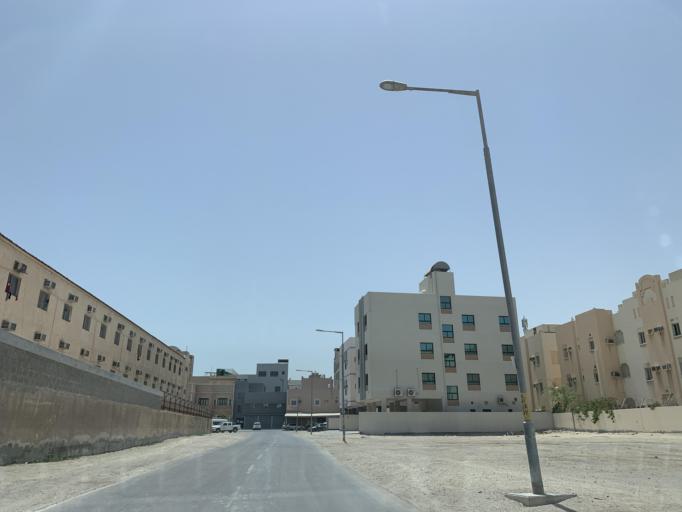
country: BH
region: Northern
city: Sitrah
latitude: 26.1421
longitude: 50.5973
